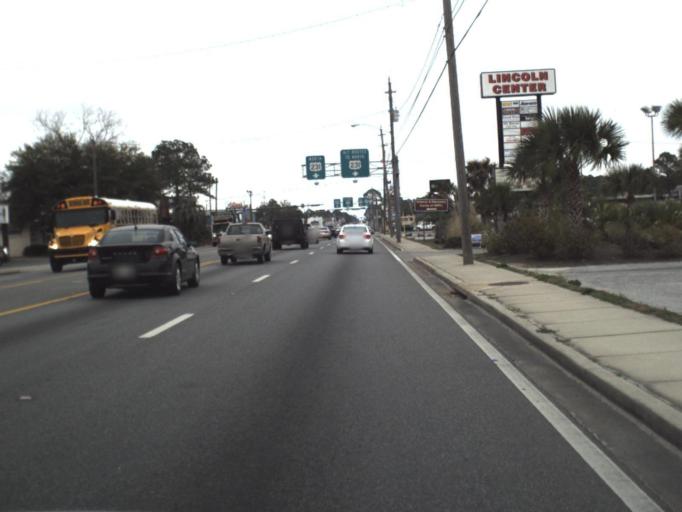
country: US
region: Florida
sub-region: Bay County
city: Panama City
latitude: 30.1751
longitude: -85.6645
